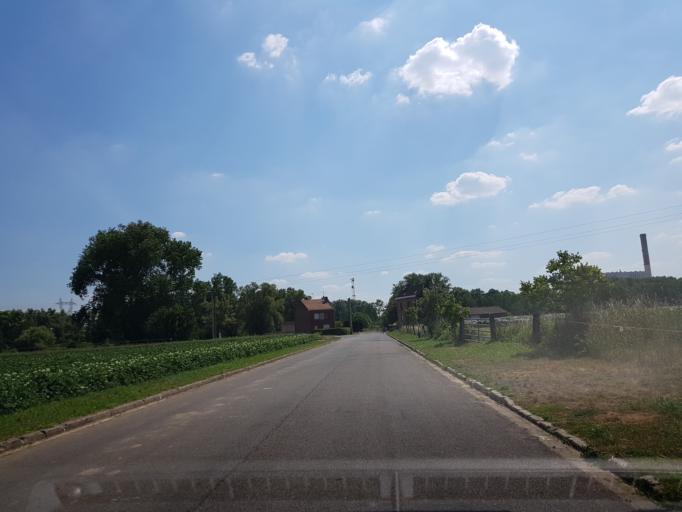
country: FR
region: Nord-Pas-de-Calais
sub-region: Departement du Nord
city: Roeulx
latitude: 50.3034
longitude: 3.3268
